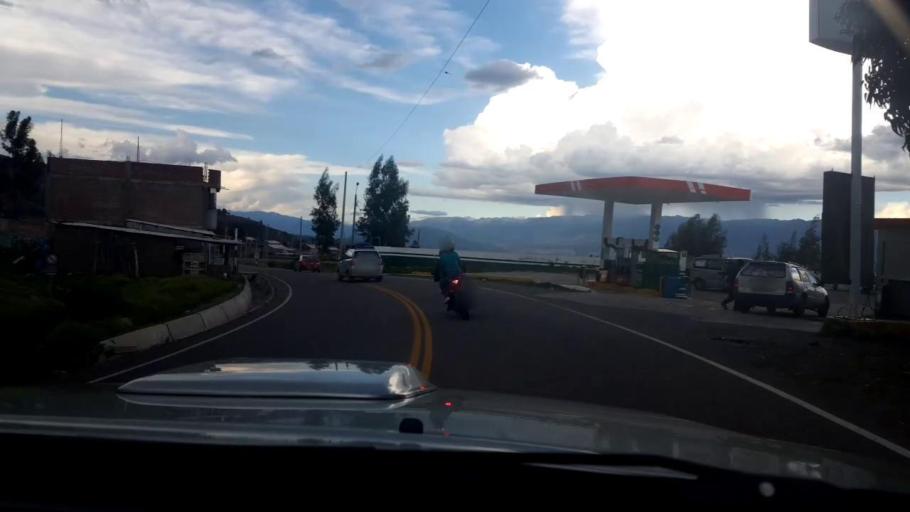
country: PE
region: Ayacucho
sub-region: Provincia de Huamanga
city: Carmen Alto
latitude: -13.2255
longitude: -74.2256
